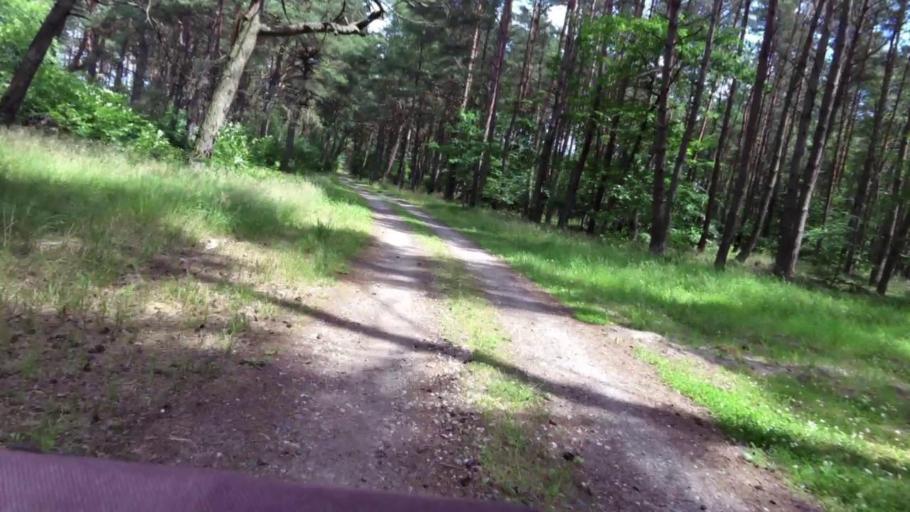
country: PL
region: West Pomeranian Voivodeship
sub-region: Powiat gryficki
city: Mrzezyno
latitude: 54.1253
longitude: 15.2403
